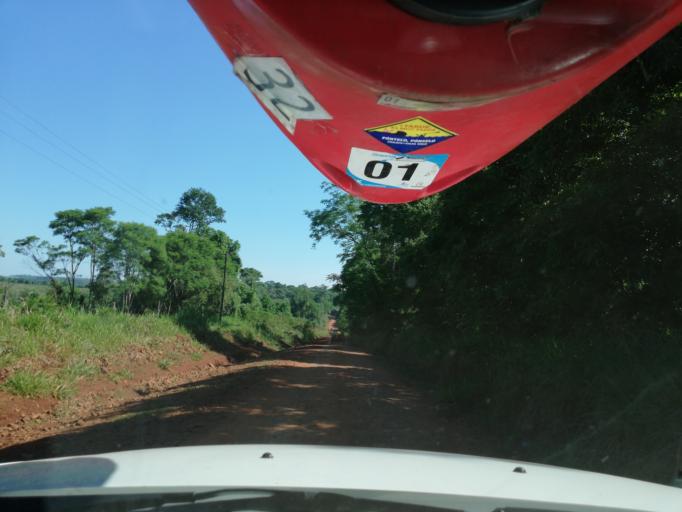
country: AR
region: Misiones
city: Puerto Leoni
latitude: -26.9737
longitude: -55.1646
